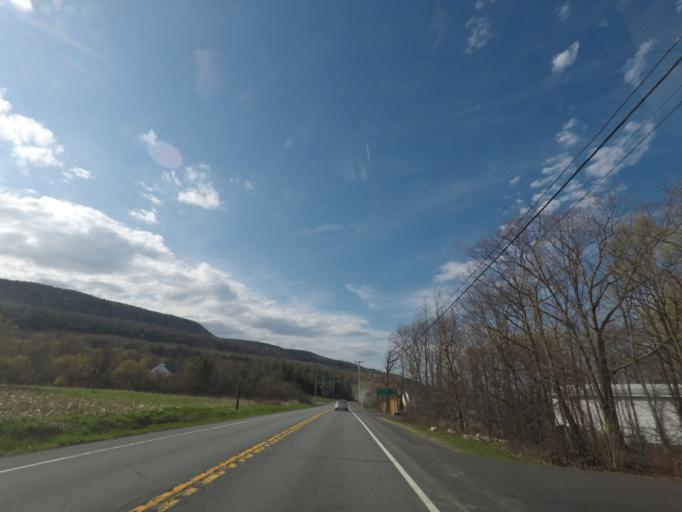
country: US
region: New York
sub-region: Albany County
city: Voorheesville
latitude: 42.6138
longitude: -73.9736
